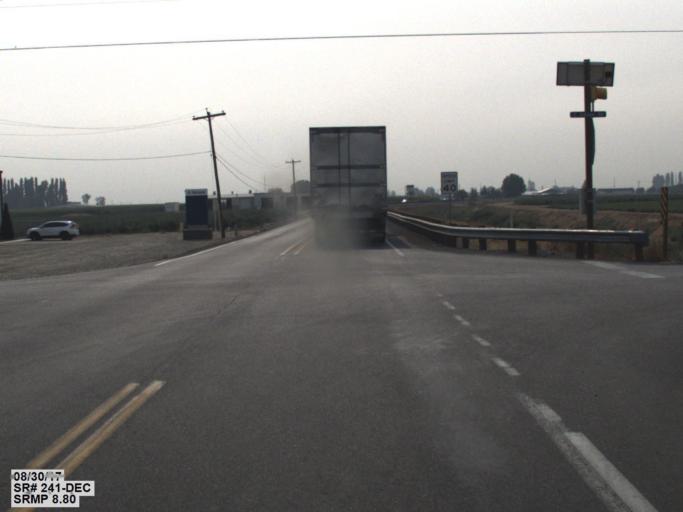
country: US
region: Washington
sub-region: Yakima County
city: Sunnyside
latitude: 46.3245
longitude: -119.9786
